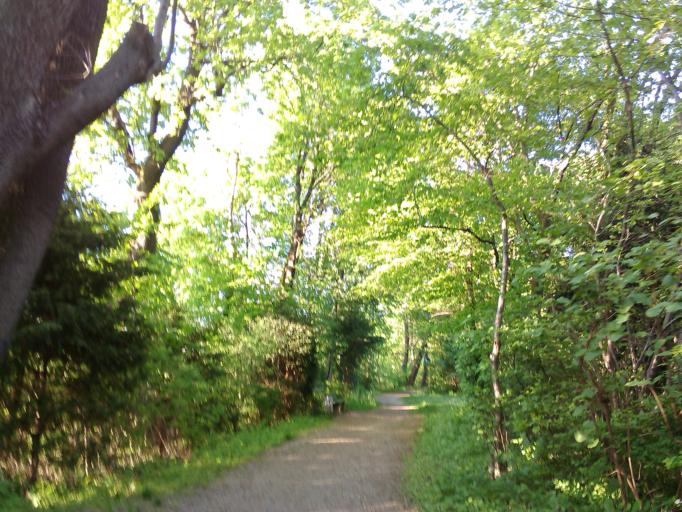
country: DE
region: Bavaria
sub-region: Upper Bavaria
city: Bogenhausen
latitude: 48.1511
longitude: 11.6079
